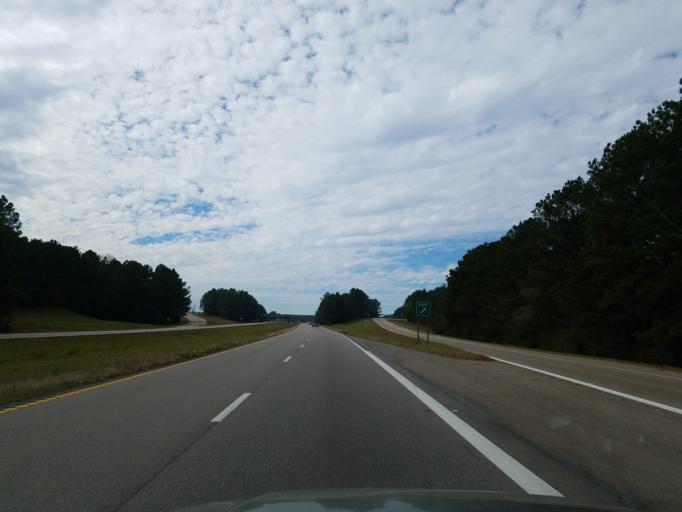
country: US
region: Mississippi
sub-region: Forrest County
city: Hattiesburg
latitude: 31.2420
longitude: -89.2967
